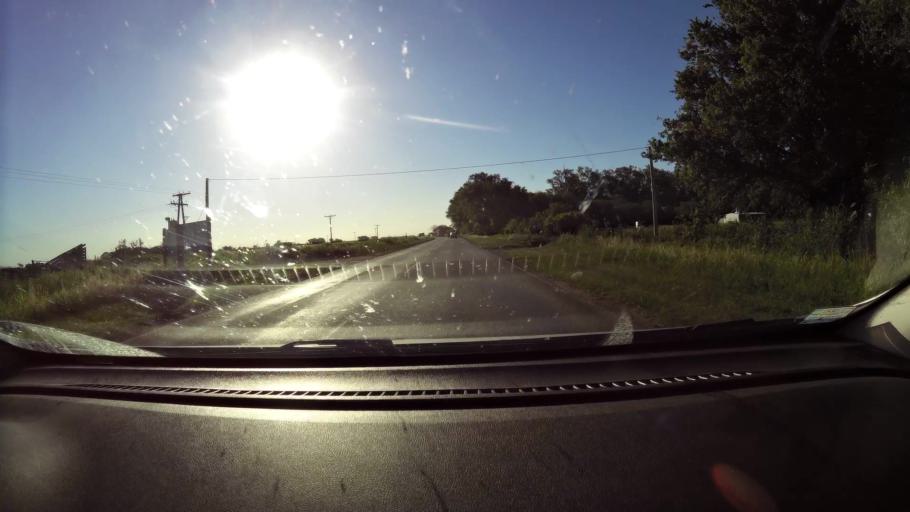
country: AR
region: Cordoba
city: Devoto
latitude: -31.5535
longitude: -62.2308
